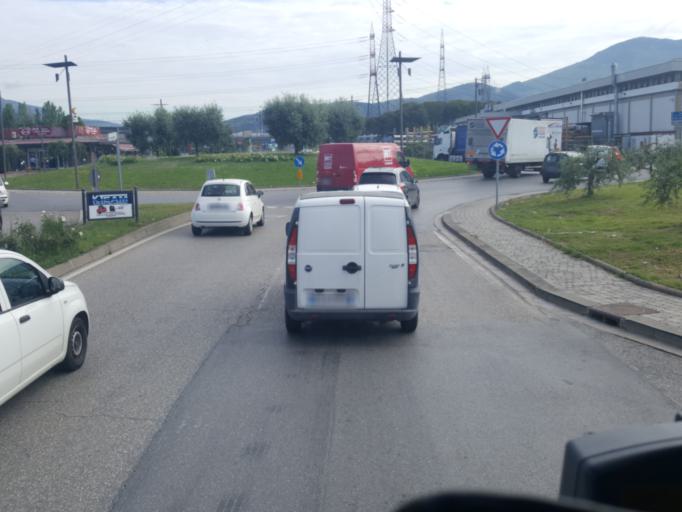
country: IT
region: Tuscany
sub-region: Province of Florence
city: Calenzano
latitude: 43.8472
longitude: 11.1612
